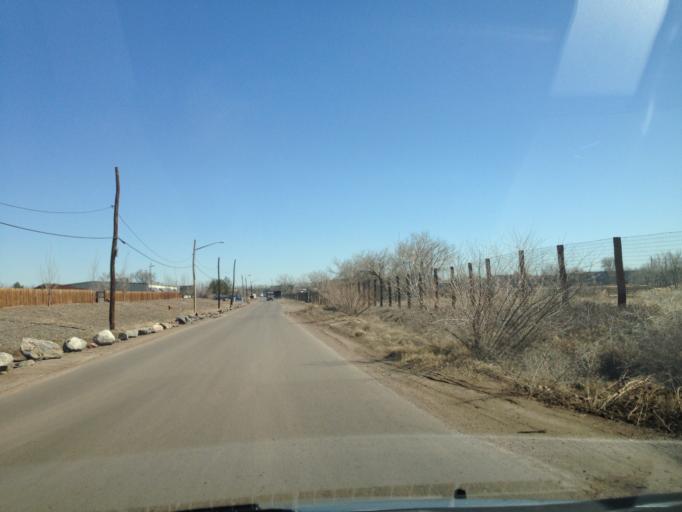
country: US
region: Colorado
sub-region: Adams County
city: Twin Lakes
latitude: 39.7956
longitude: -104.9758
